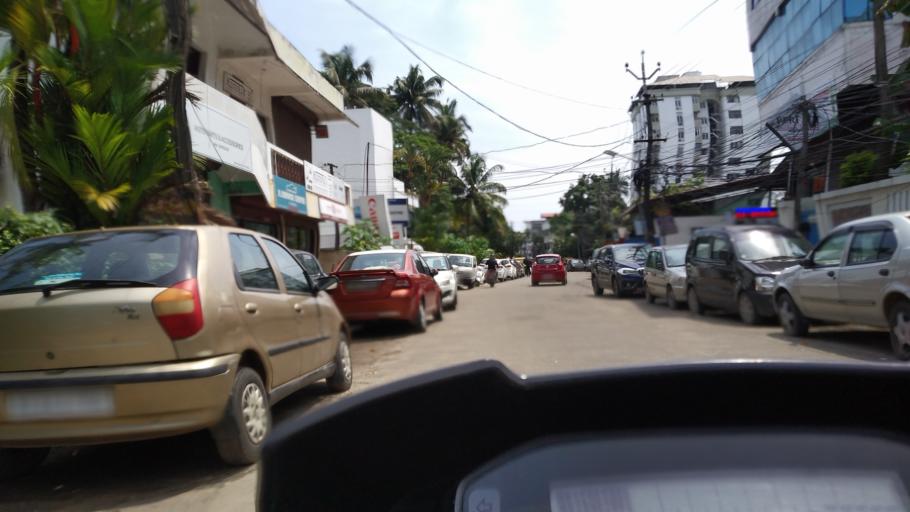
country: IN
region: Kerala
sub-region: Ernakulam
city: Cochin
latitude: 9.9576
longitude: 76.2924
